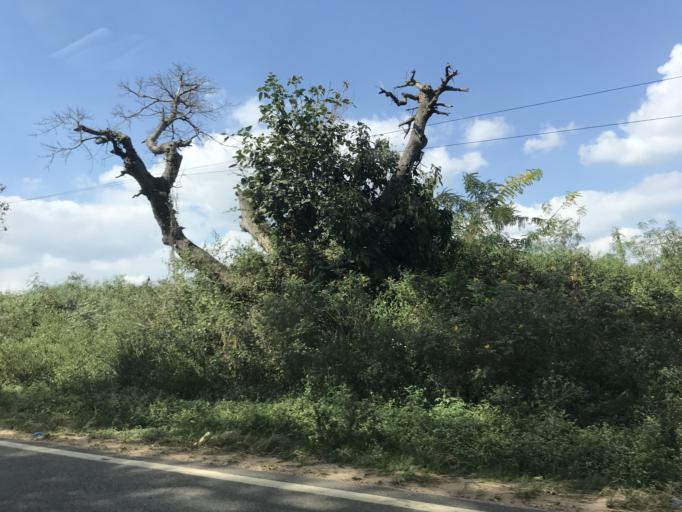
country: IN
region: Karnataka
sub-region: Hassan
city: Hassan
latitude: 12.9933
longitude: 76.0664
